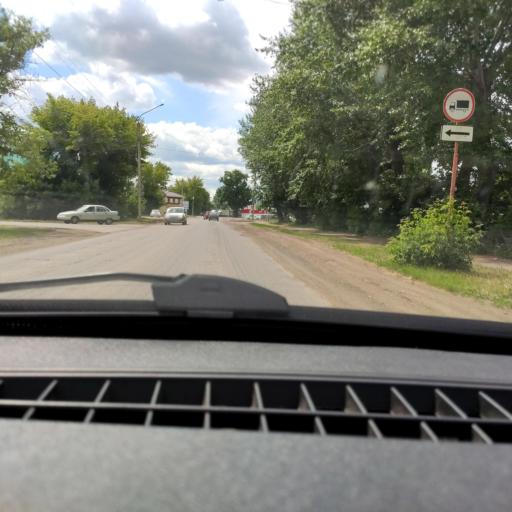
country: RU
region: Bashkortostan
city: Sterlitamak
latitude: 53.6519
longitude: 55.9420
